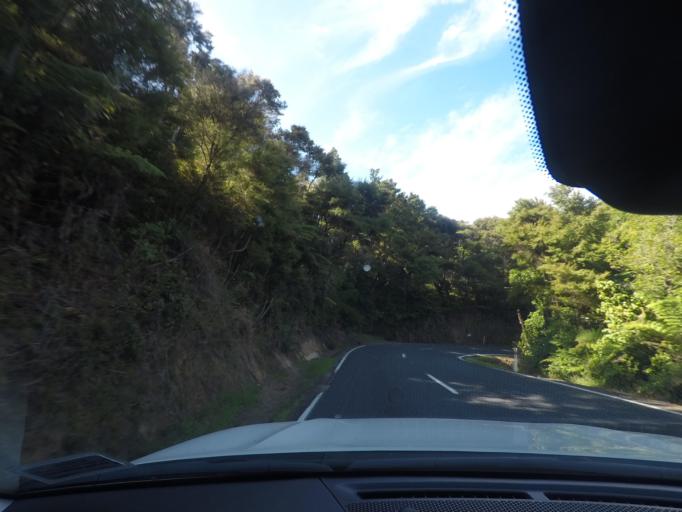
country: NZ
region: Northland
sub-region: Whangarei
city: Ngunguru
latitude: -35.6672
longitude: 174.4700
